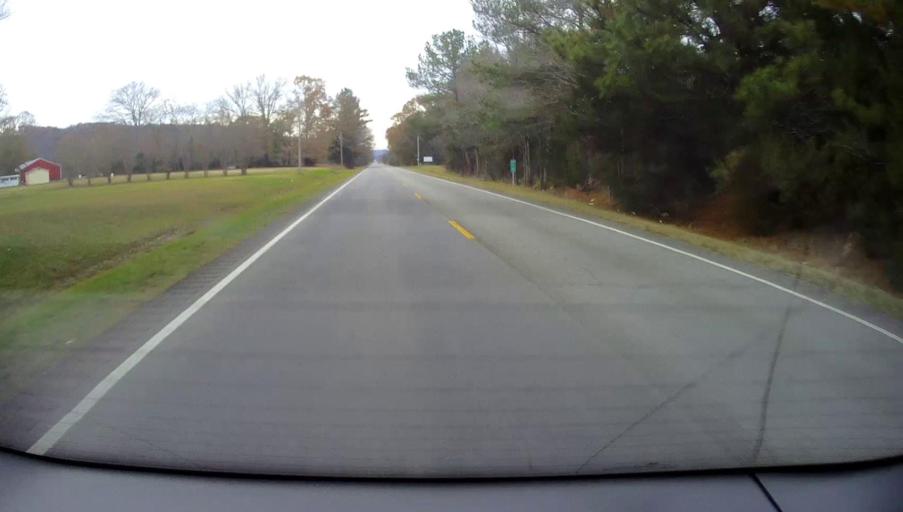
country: US
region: Alabama
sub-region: Marshall County
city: Arab
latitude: 34.3924
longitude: -86.6722
